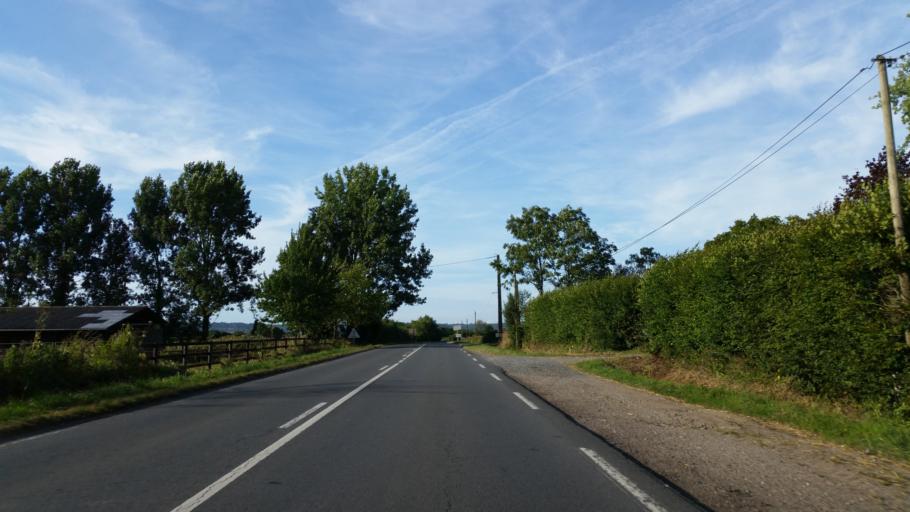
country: FR
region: Lower Normandy
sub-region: Departement du Calvados
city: Cambremer
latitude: 49.1528
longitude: -0.0077
